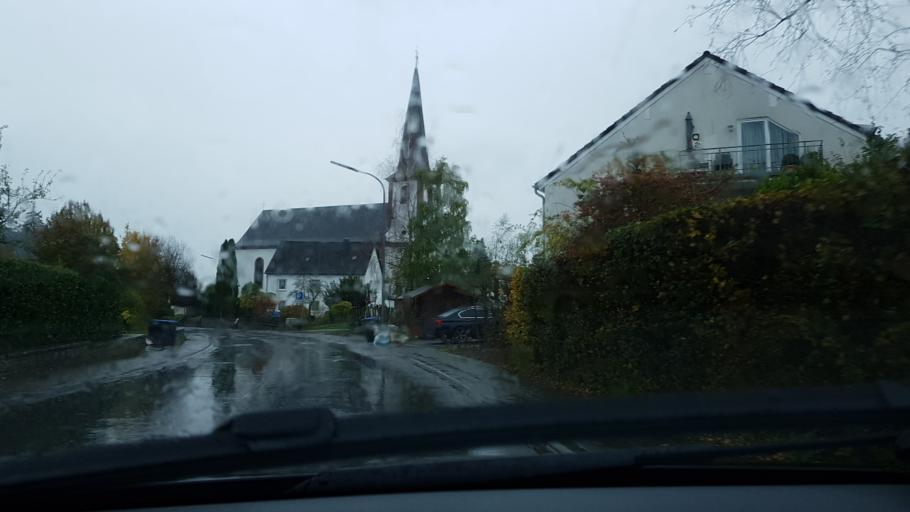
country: DE
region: Rheinland-Pfalz
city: Neuerburg
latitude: 49.9894
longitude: 6.9390
